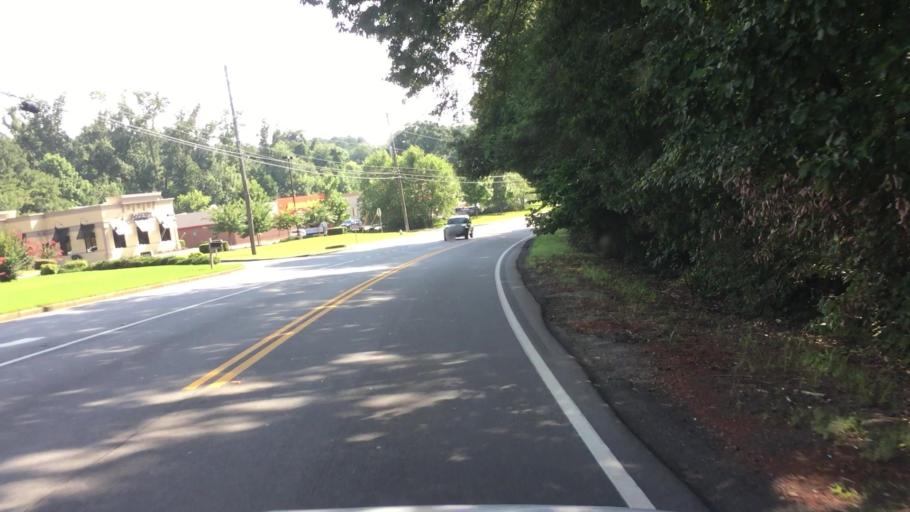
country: US
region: Georgia
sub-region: Gwinnett County
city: Dacula
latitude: 33.9888
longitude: -83.8906
